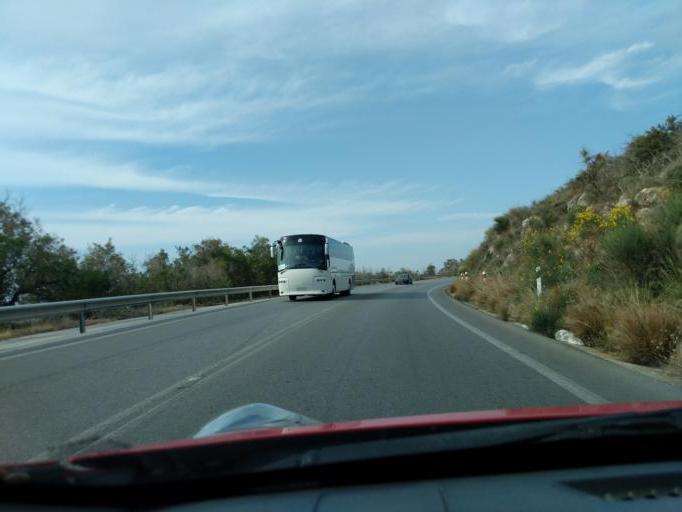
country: GR
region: Crete
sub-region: Nomos Rethymnis
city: Atsipopoulon
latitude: 35.3589
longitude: 24.3723
